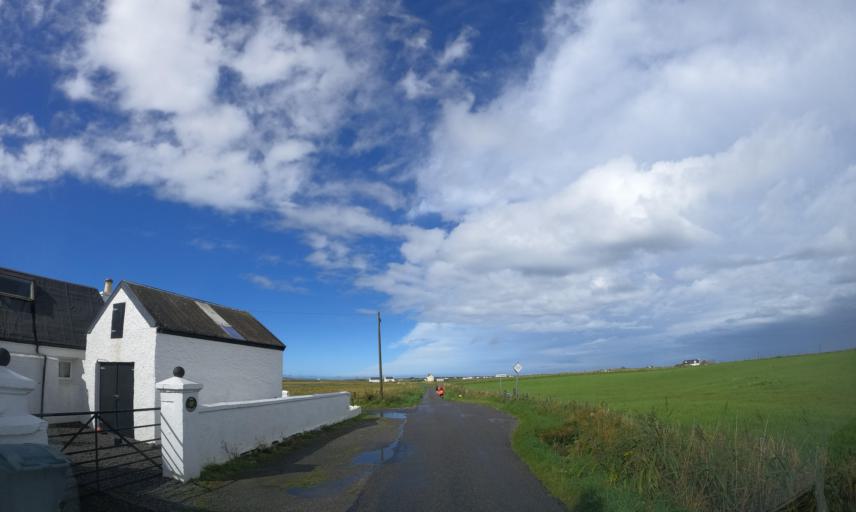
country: GB
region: Scotland
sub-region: Eilean Siar
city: Barra
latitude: 56.5209
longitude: -6.8965
